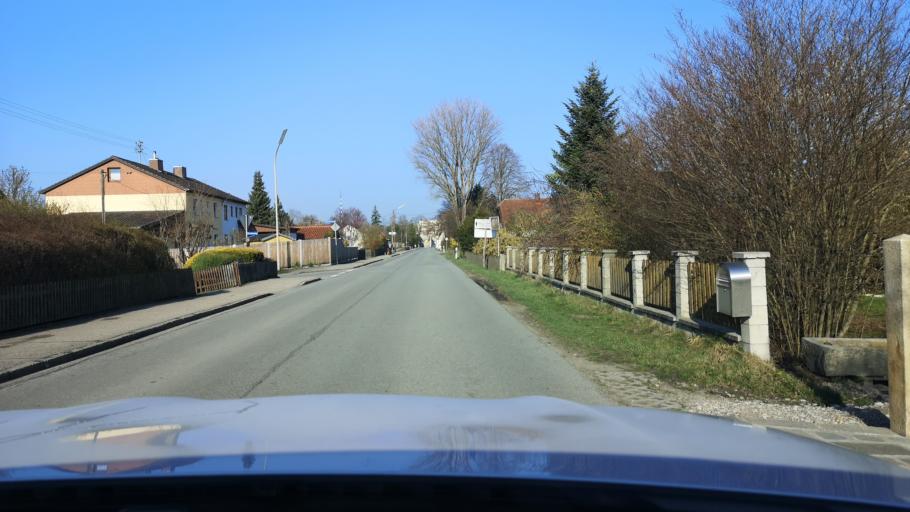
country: DE
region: Bavaria
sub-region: Upper Bavaria
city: Finsing
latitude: 48.2200
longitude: 11.8071
